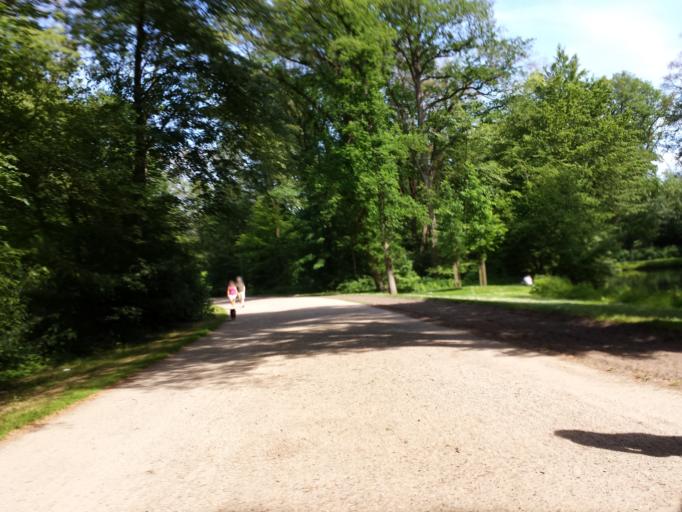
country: DE
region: Bremen
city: Bremen
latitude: 53.1014
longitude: 8.8324
